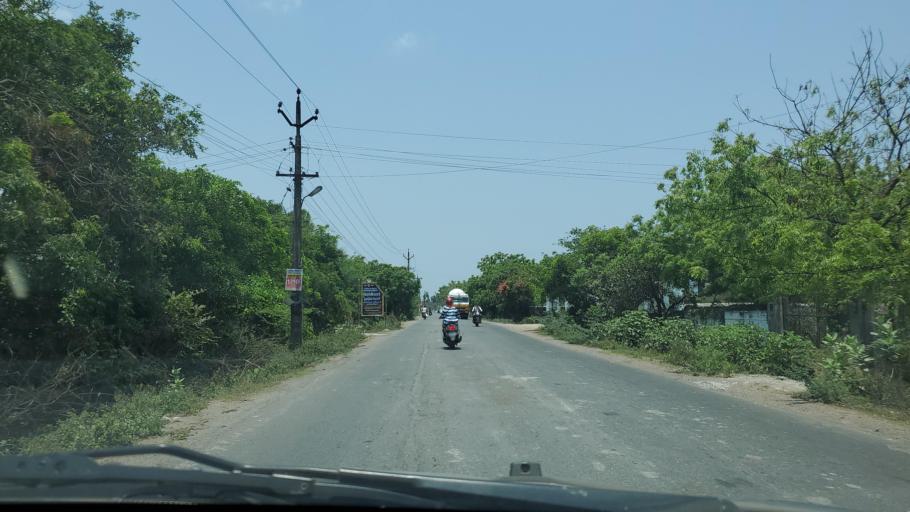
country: IN
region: Tamil Nadu
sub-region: Kancheepuram
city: Vengavasal
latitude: 12.8487
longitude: 80.1705
